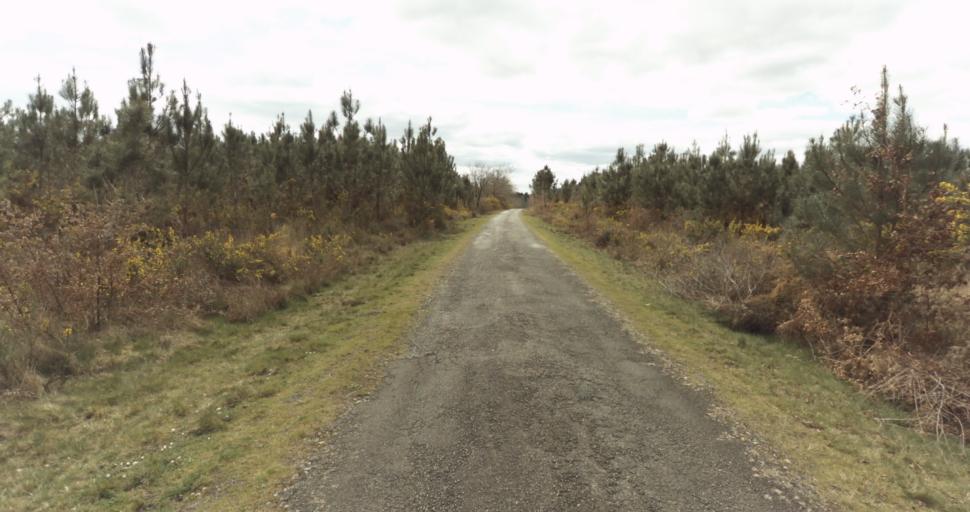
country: FR
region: Aquitaine
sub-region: Departement des Landes
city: Roquefort
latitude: 44.0919
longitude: -0.4403
